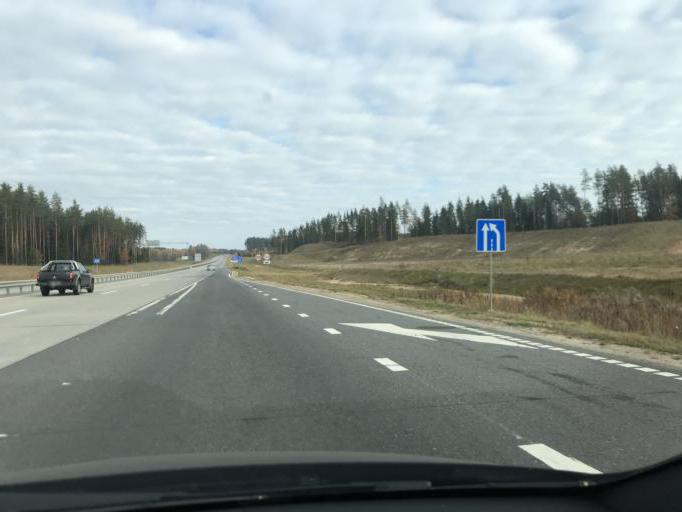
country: BY
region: Minsk
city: Rakaw
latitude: 53.9689
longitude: 27.0911
